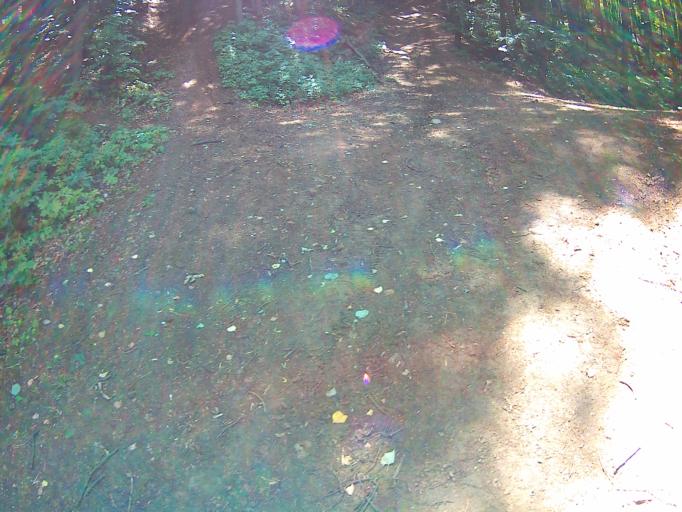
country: RU
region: Nizjnij Novgorod
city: Nizhniy Novgorod
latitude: 56.2392
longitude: 43.9390
